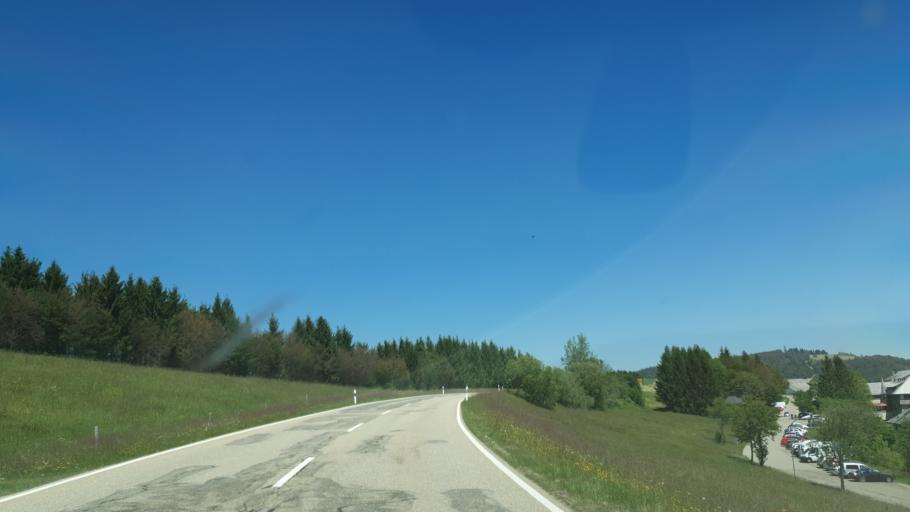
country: DE
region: Baden-Wuerttemberg
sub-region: Freiburg Region
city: Wieden
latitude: 47.8886
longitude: 7.8916
